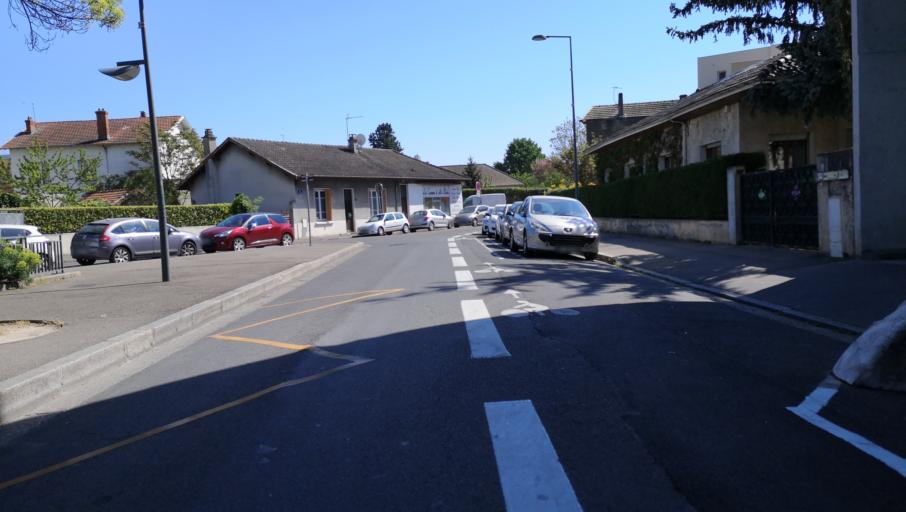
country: FR
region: Rhone-Alpes
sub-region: Departement du Rhone
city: Bron
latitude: 45.7513
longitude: 4.9147
